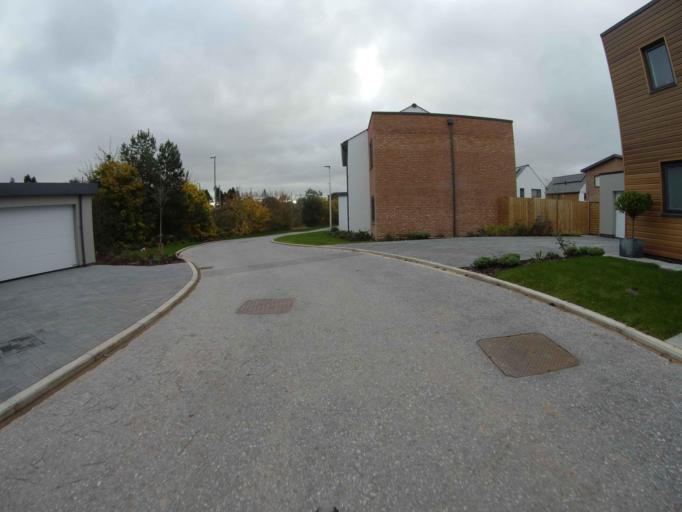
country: GB
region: England
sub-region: Devon
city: Topsham
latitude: 50.7006
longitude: -3.4770
